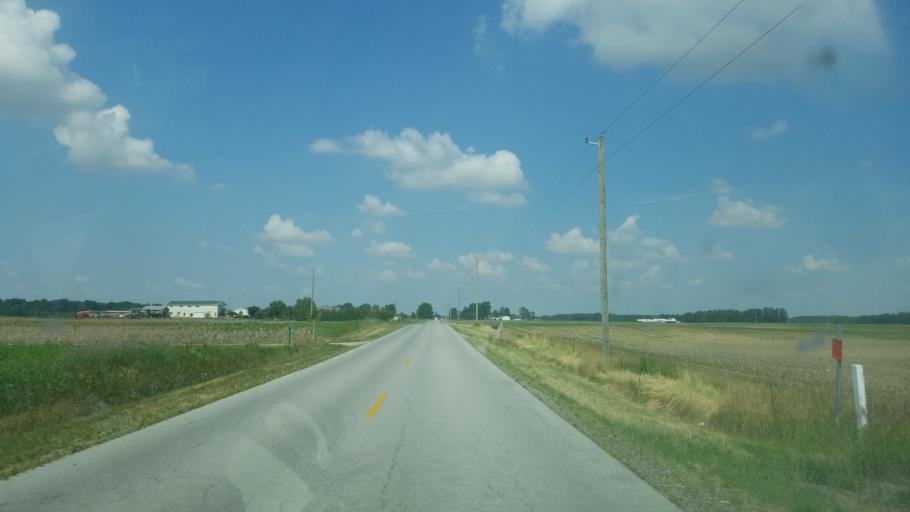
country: US
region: Ohio
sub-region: Auglaize County
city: Wapakoneta
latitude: 40.5703
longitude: -84.1407
